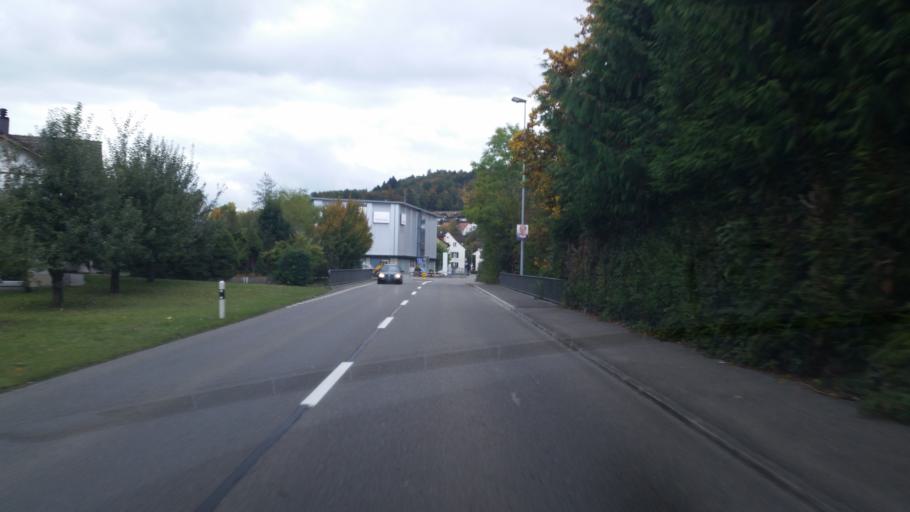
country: CH
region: Aargau
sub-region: Bezirk Zurzach
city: Oberendingen
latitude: 47.5392
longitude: 8.2900
